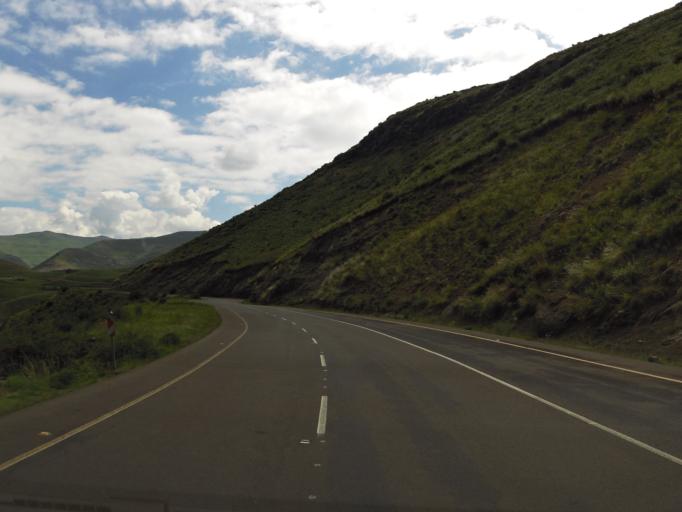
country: LS
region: Thaba-Tseka
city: Thaba-Tseka
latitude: -29.1490
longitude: 28.4864
